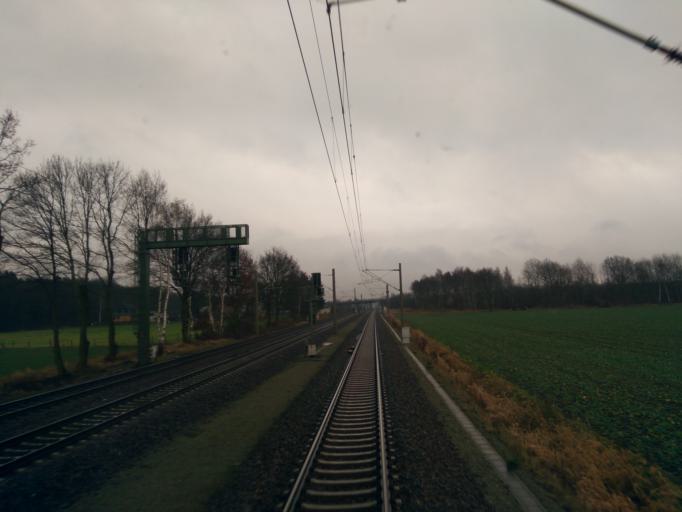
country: DE
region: Lower Saxony
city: Winsen
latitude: 53.3386
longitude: 10.2405
